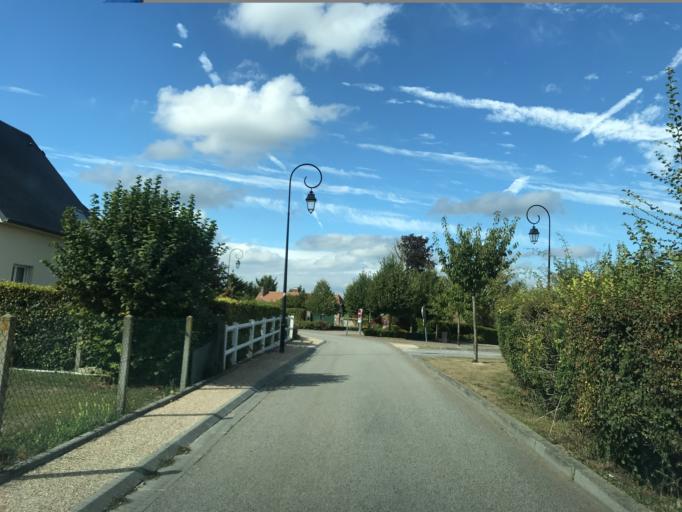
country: FR
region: Haute-Normandie
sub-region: Departement de l'Eure
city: Saint-Pierre-du-Vauvray
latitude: 49.2079
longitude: 1.2290
